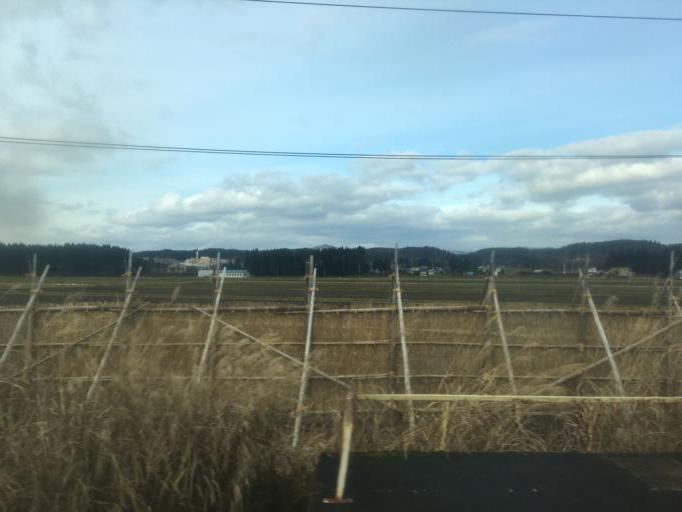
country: JP
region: Akita
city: Takanosu
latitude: 40.2504
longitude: 140.3971
